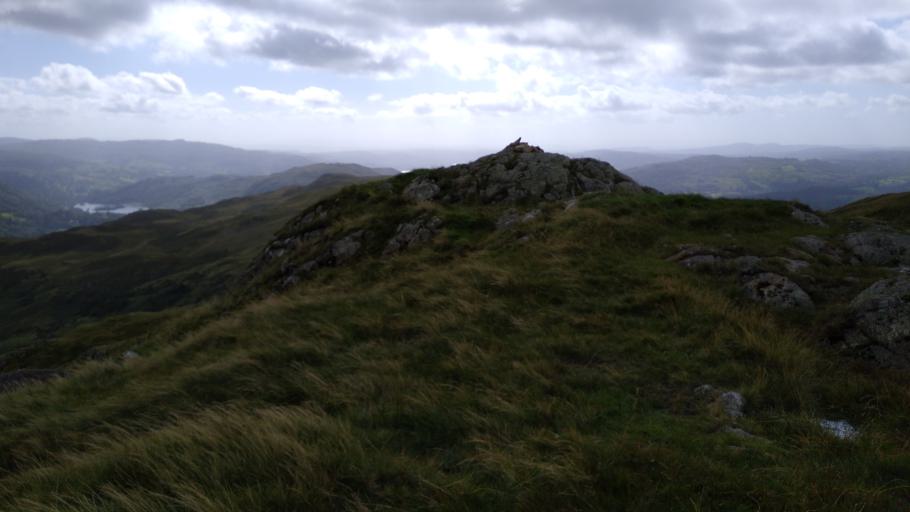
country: GB
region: England
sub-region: Cumbria
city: Ambleside
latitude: 54.4592
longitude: -3.0660
